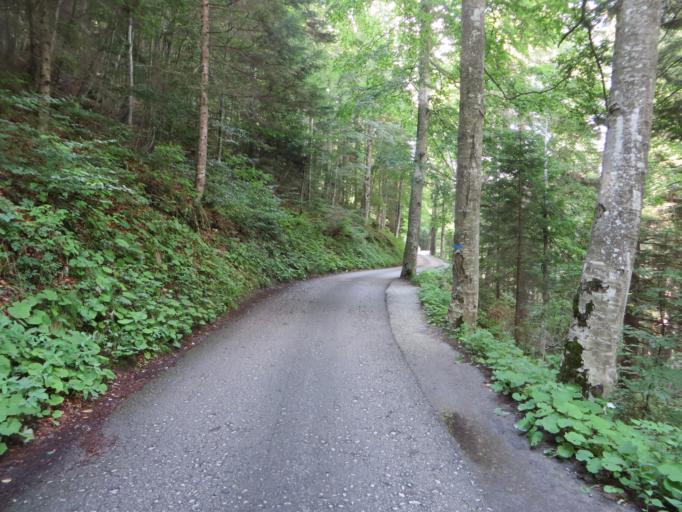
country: IT
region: Trentino-Alto Adige
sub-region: Provincia di Trento
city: Carisolo
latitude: 46.2163
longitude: 10.8283
